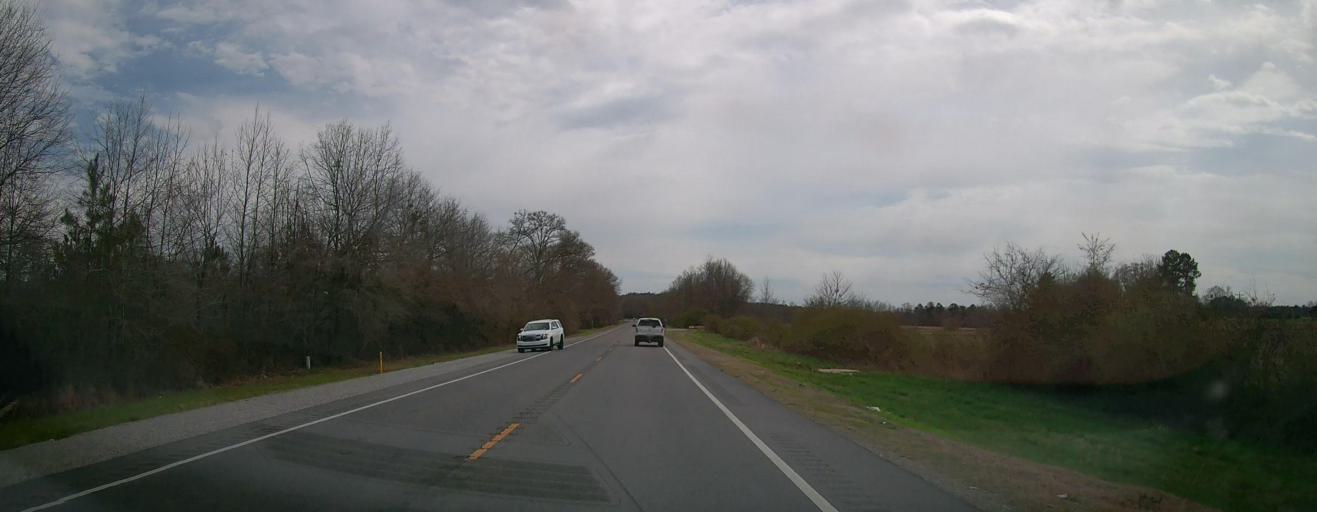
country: US
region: Alabama
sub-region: Marion County
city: Guin
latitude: 34.0025
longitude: -87.9321
